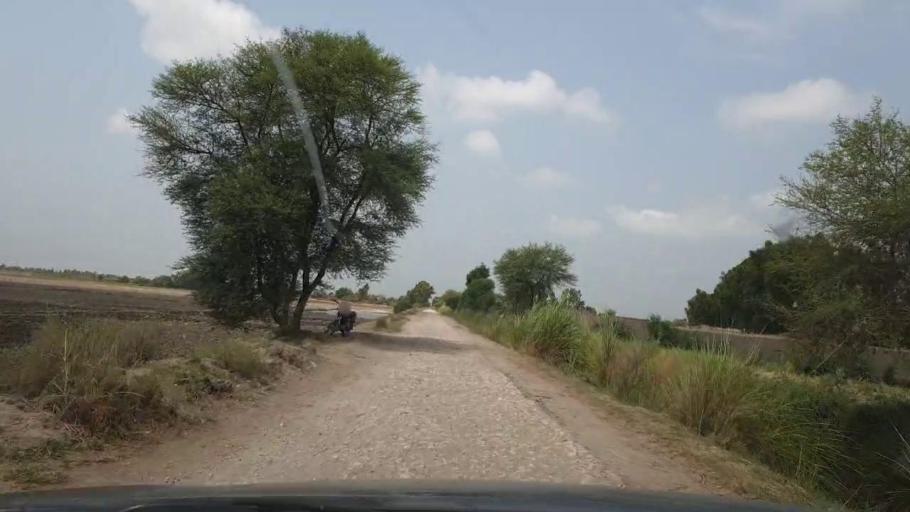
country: PK
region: Sindh
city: Ratodero
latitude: 27.8912
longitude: 68.2989
